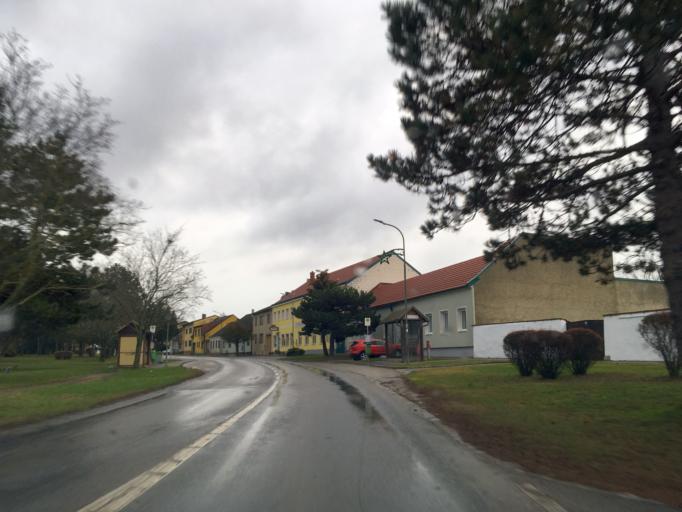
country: AT
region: Lower Austria
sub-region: Politischer Bezirk Wien-Umgebung
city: Rauchenwarth
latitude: 48.0836
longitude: 16.5307
